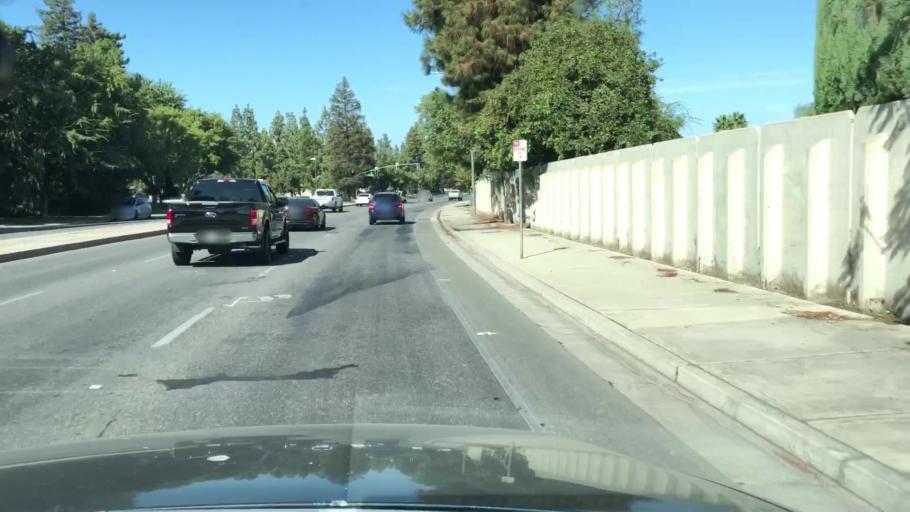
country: US
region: California
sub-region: Kern County
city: Greenacres
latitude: 35.3350
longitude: -119.0778
